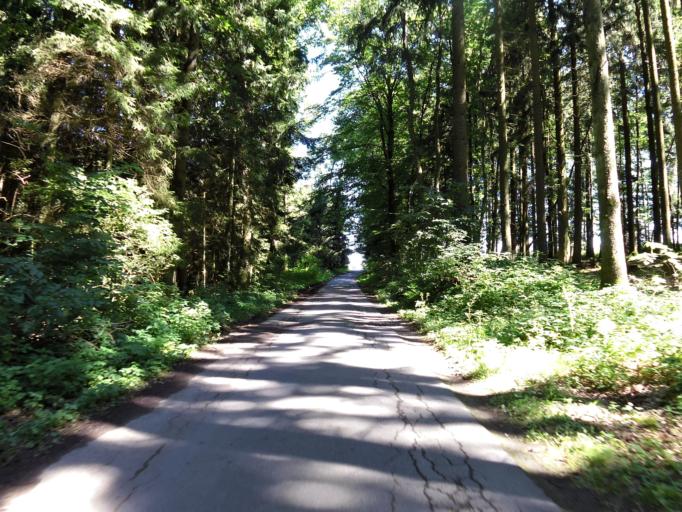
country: DE
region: Hesse
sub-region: Regierungsbezirk Darmstadt
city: Erbach
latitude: 49.6506
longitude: 8.9494
